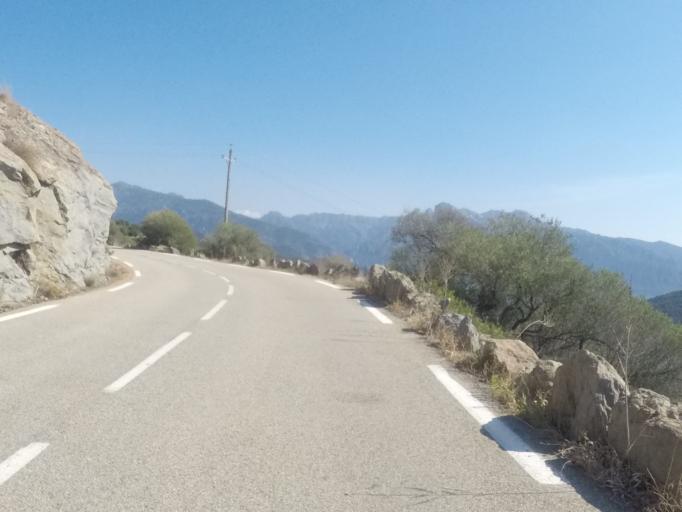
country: FR
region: Corsica
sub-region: Departement de la Corse-du-Sud
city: Cargese
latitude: 42.3250
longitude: 8.6354
